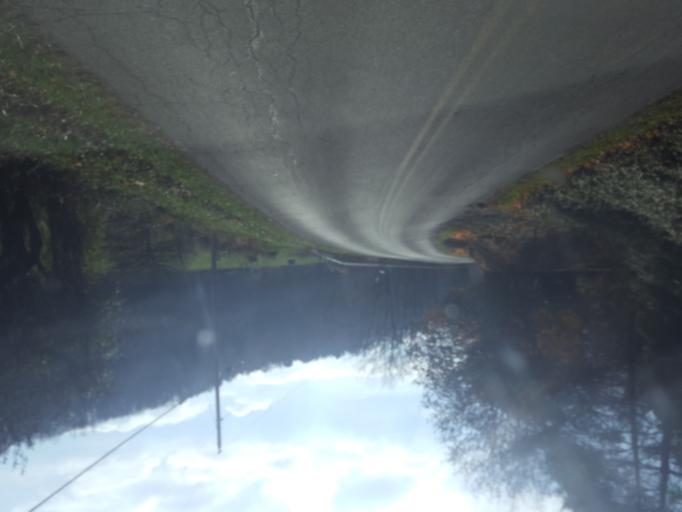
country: US
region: Ohio
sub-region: Ashland County
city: Loudonville
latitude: 40.5276
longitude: -82.1030
